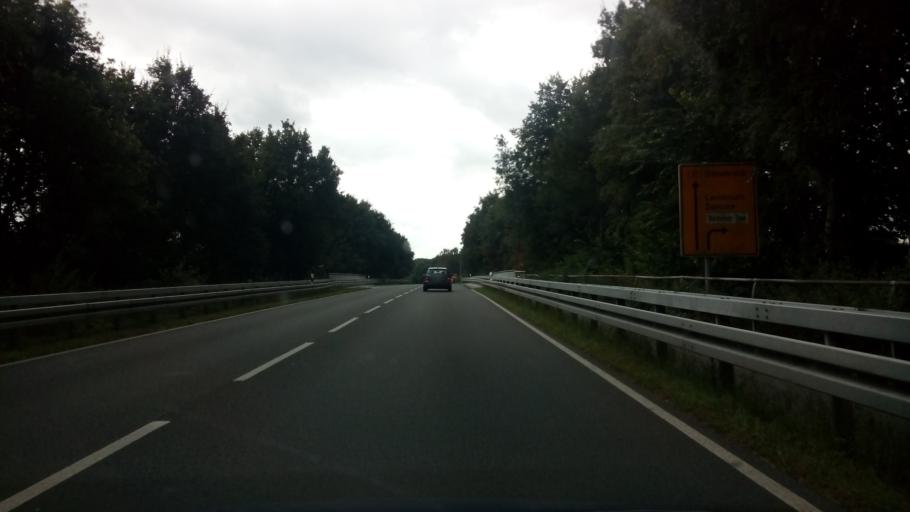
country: DE
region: Lower Saxony
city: Lembruch
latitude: 52.5225
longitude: 8.3743
